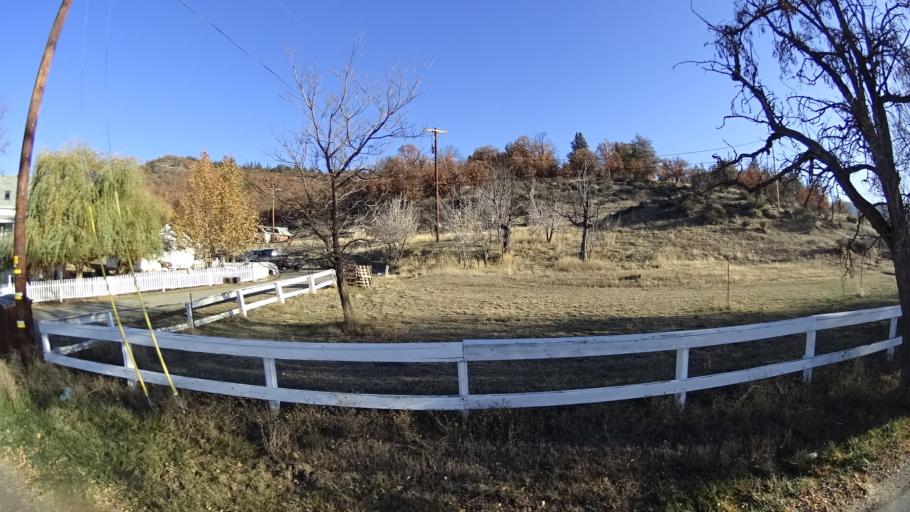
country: US
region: Oregon
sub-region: Jackson County
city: Ashland
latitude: 42.0022
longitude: -122.6408
